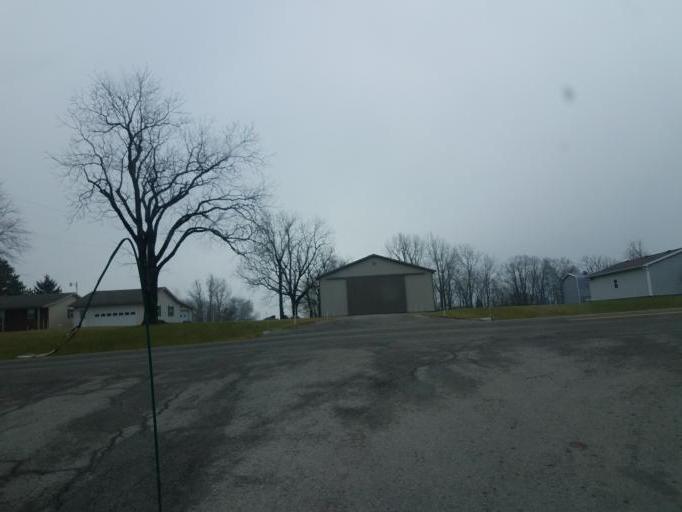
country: US
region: Ohio
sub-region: Champaign County
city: North Lewisburg
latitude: 40.2813
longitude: -83.5961
